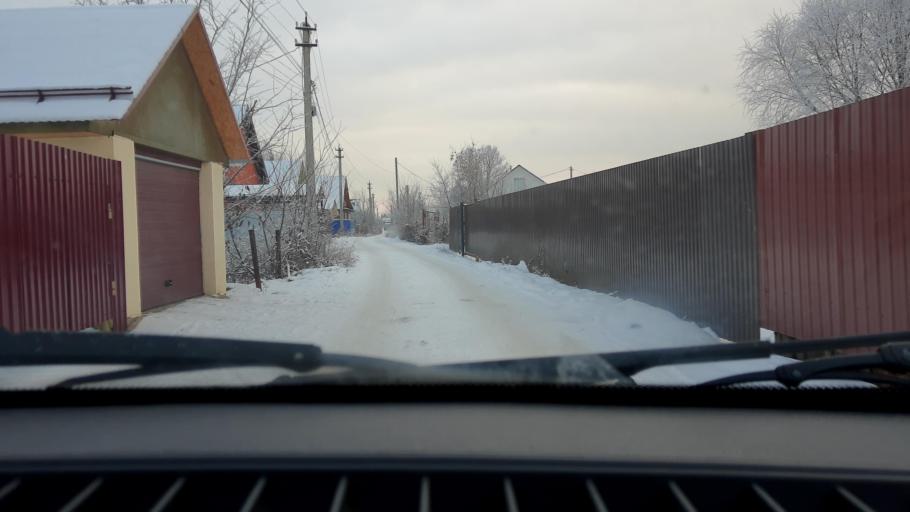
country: RU
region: Bashkortostan
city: Ufa
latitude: 54.6573
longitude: 55.9251
